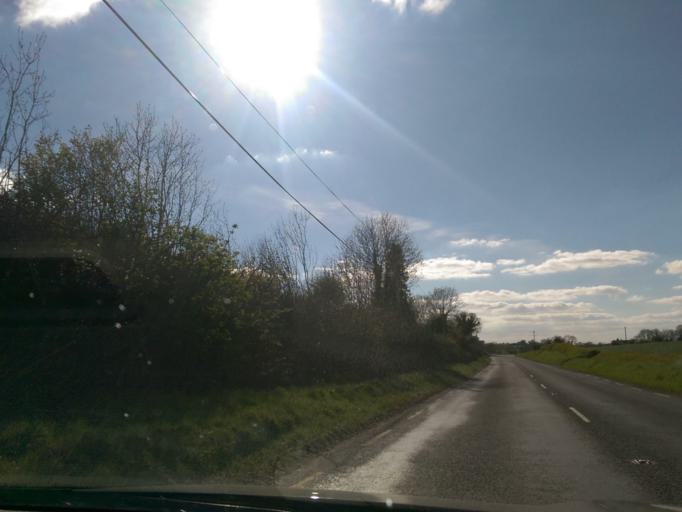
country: IE
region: Leinster
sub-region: Uibh Fhaili
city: Banagher
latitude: 53.1018
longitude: -8.0022
